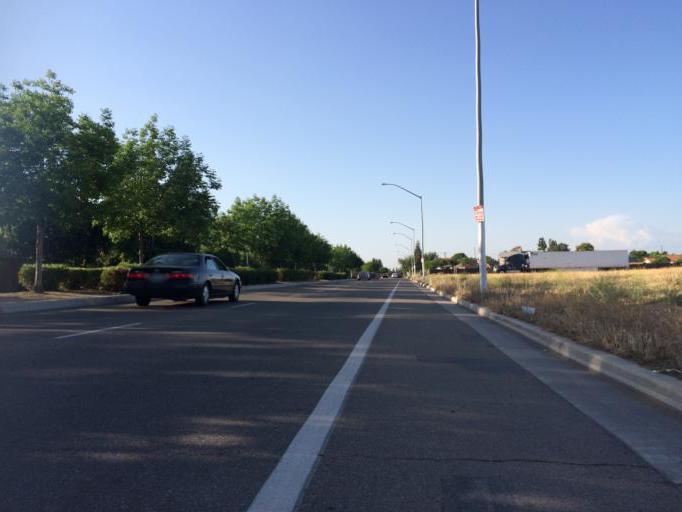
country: US
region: California
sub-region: Fresno County
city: Sunnyside
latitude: 36.7582
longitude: -119.7182
